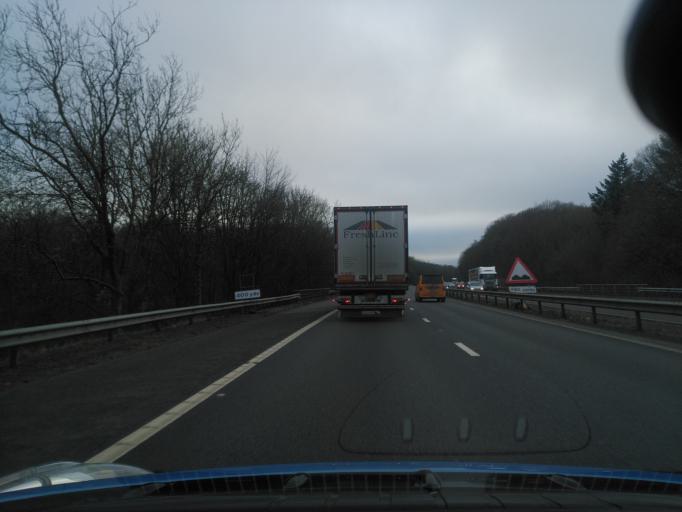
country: GB
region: England
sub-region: Hertfordshire
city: Knebworth
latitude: 51.8529
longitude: -0.1959
